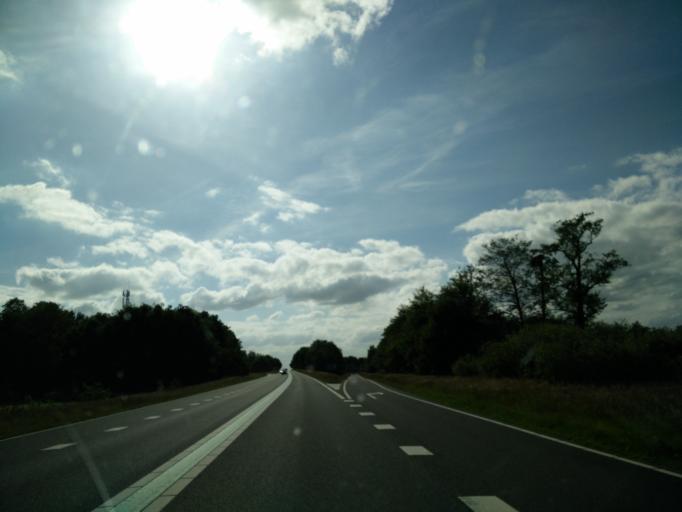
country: NL
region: Drenthe
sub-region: Gemeente Coevorden
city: Sleen
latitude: 52.8023
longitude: 6.7391
